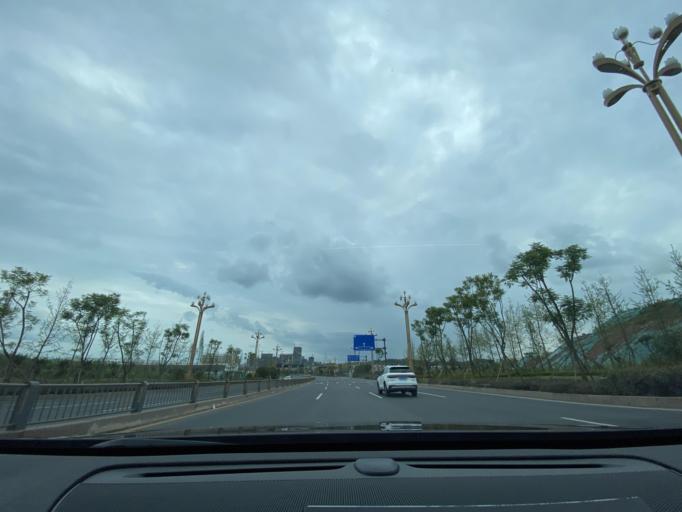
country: CN
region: Sichuan
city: Jiancheng
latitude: 30.4452
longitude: 104.4960
